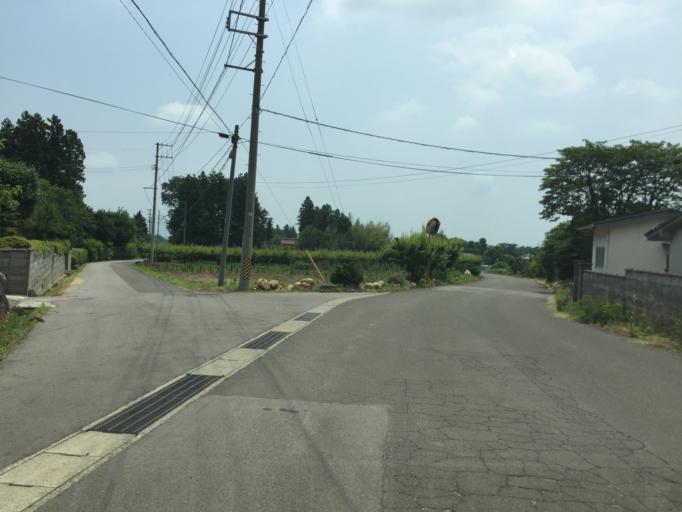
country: JP
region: Fukushima
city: Fukushima-shi
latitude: 37.7698
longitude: 140.3669
